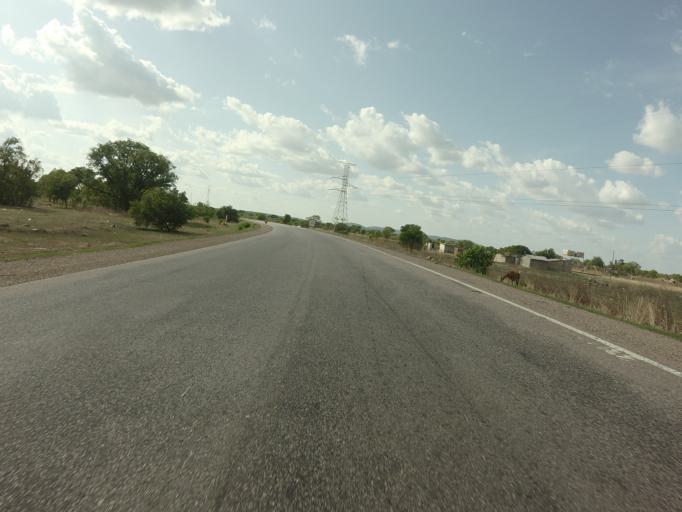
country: GH
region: Upper East
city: Bolgatanga
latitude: 10.5804
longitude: -0.8321
